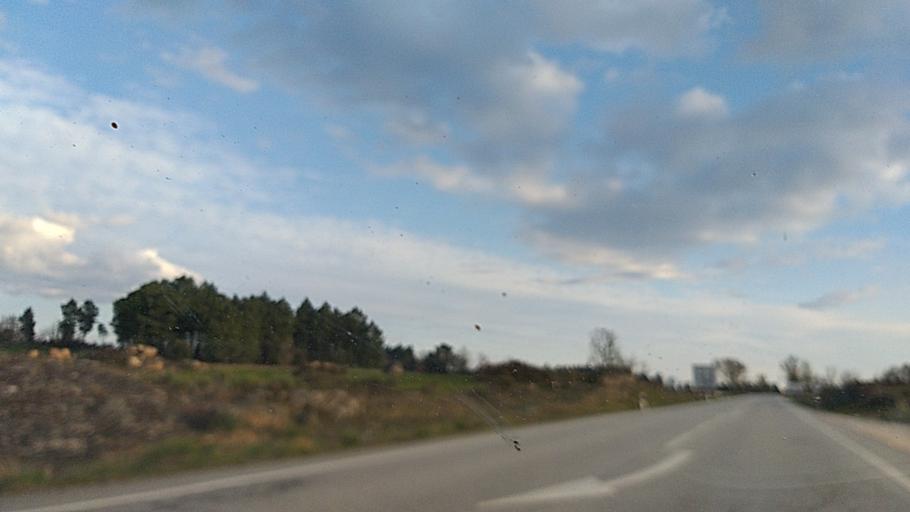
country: PT
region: Guarda
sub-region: Pinhel
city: Pinhel
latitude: 40.6601
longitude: -6.9681
